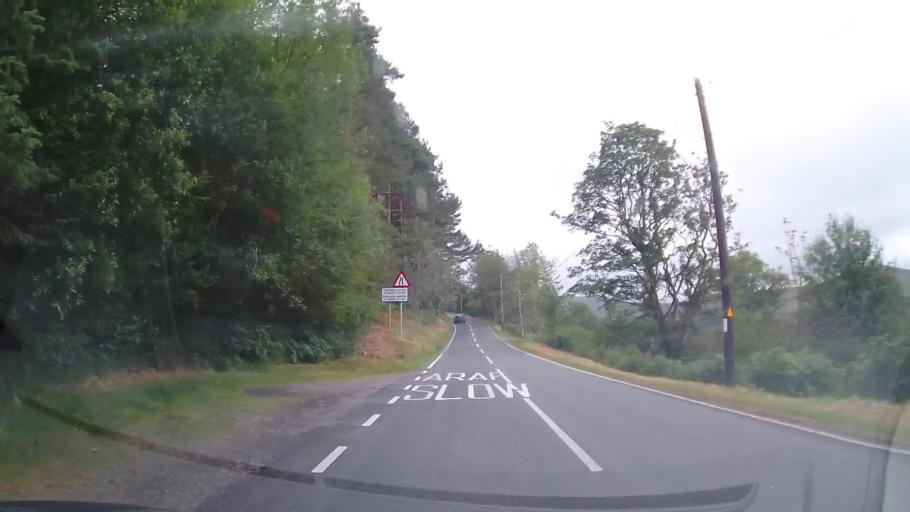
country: GB
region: Wales
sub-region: Denbighshire
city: Llandrillo
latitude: 52.9039
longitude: -3.5137
